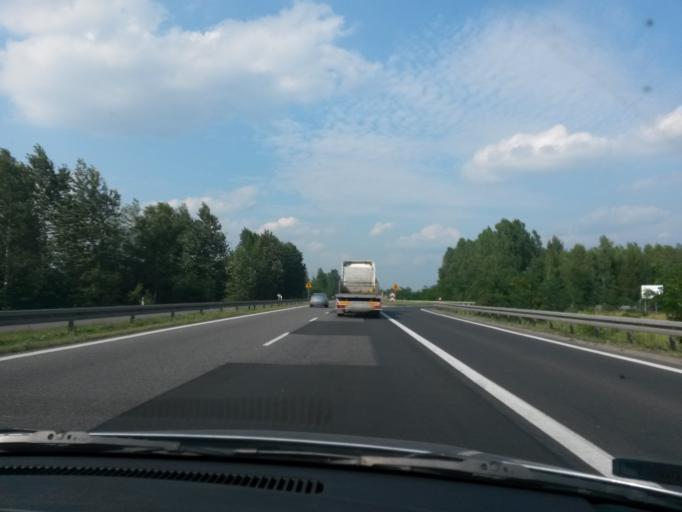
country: PL
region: Silesian Voivodeship
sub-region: Myslowice
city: Myslowice
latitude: 50.2557
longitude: 19.1861
